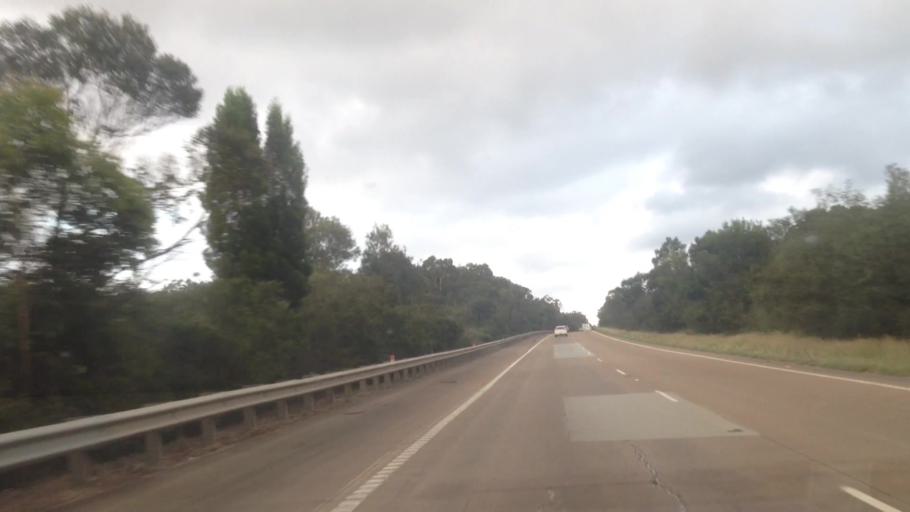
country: AU
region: New South Wales
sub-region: Wyong Shire
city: Charmhaven
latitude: -33.1553
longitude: 151.4709
